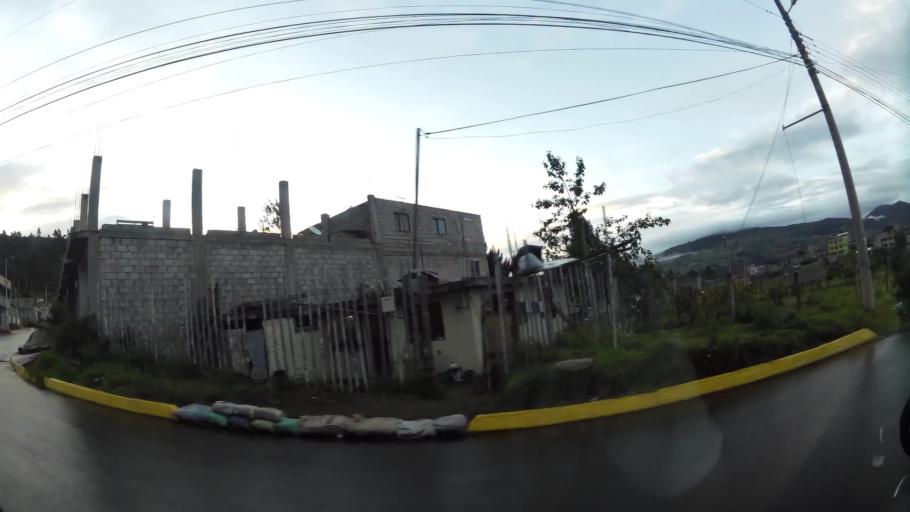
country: EC
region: Pichincha
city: Quito
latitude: -0.0965
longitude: -78.5292
